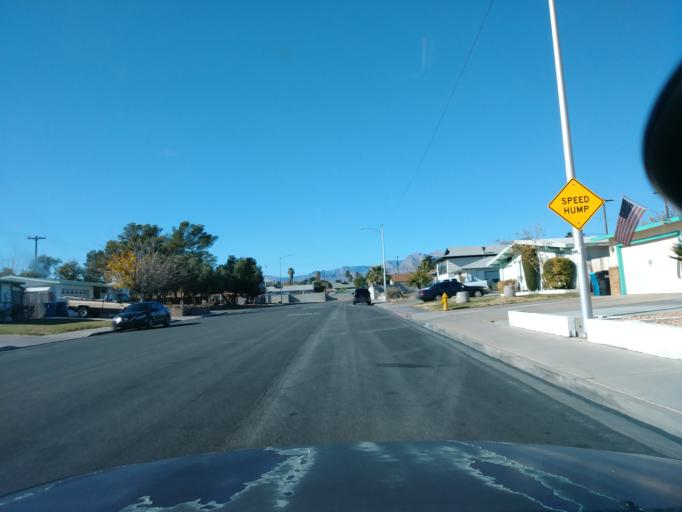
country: US
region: Nevada
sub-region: Clark County
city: Spring Valley
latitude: 36.1759
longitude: -115.2316
